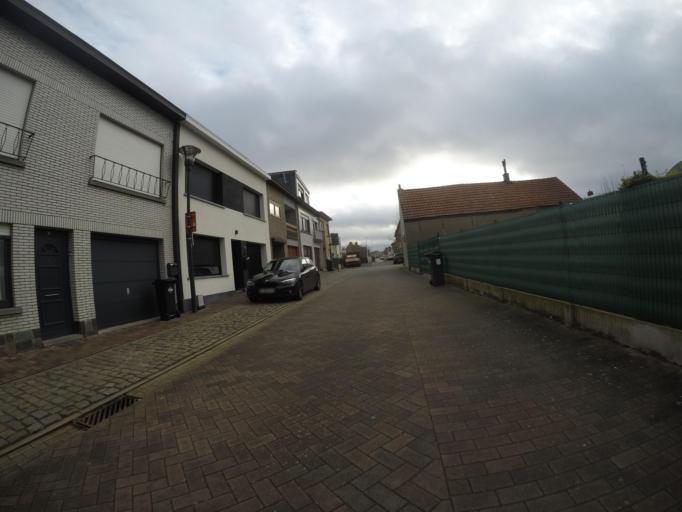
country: BE
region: Flanders
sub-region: Provincie Vlaams-Brabant
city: Liedekerke
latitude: 50.8690
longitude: 4.0820
